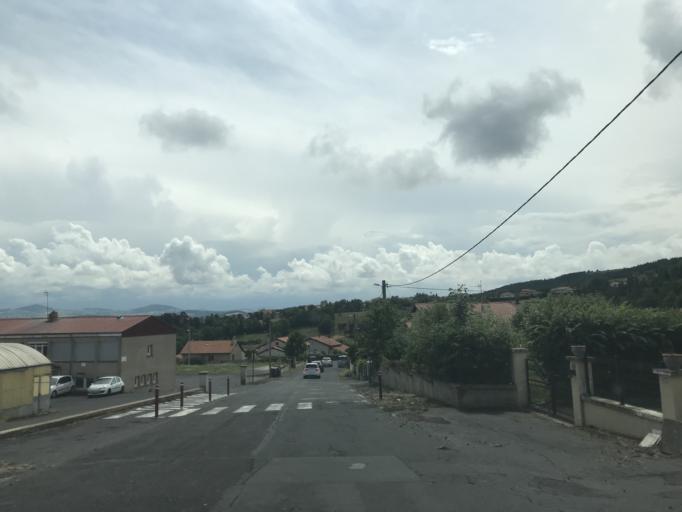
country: FR
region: Auvergne
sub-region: Departement de la Haute-Loire
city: Cussac-sur-Loire
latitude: 44.9925
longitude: 3.8684
